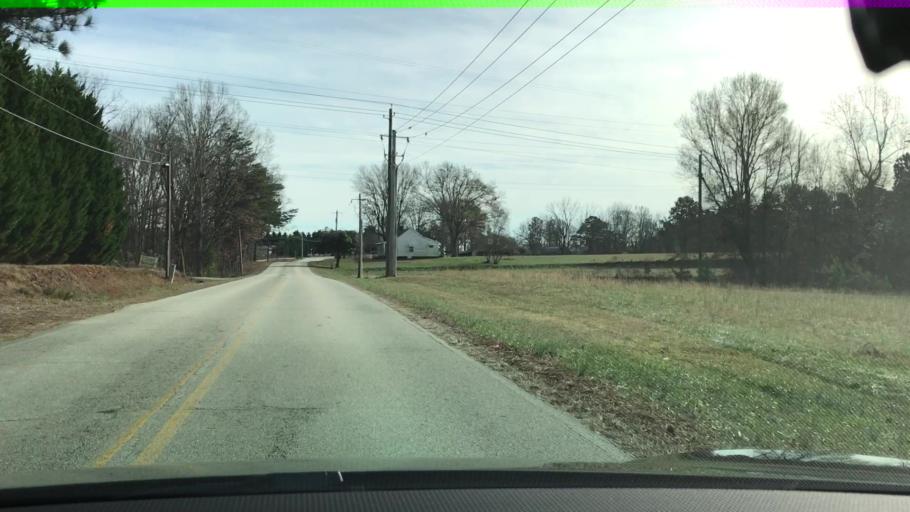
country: US
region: Georgia
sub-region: Gwinnett County
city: Buford
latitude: 34.1485
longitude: -83.9905
